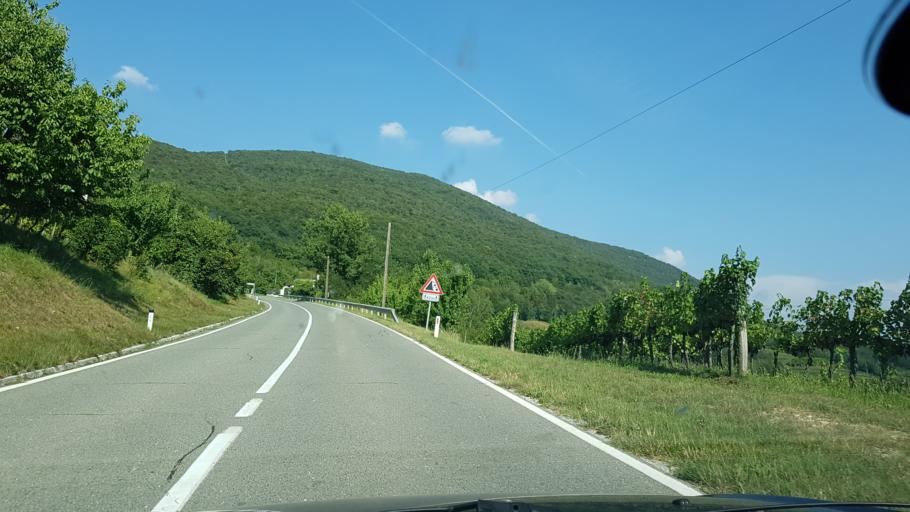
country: IT
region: Friuli Venezia Giulia
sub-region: Provincia di Gorizia
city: San Floriano del Collio
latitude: 45.9867
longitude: 13.6110
